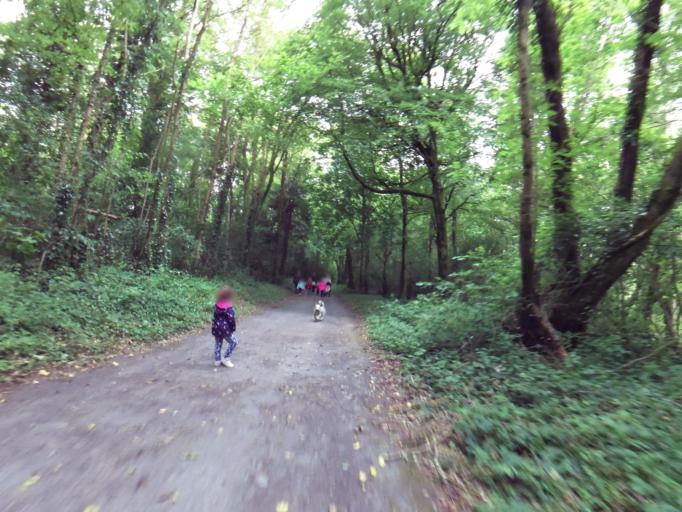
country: IE
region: Connaught
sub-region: County Galway
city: Gort
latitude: 53.0799
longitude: -8.8718
